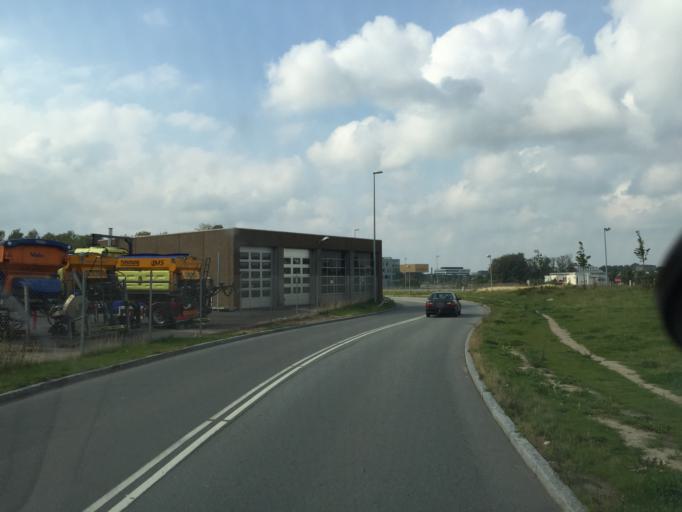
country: DK
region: Zealand
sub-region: Roskilde Kommune
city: Roskilde
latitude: 55.6234
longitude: 12.0911
